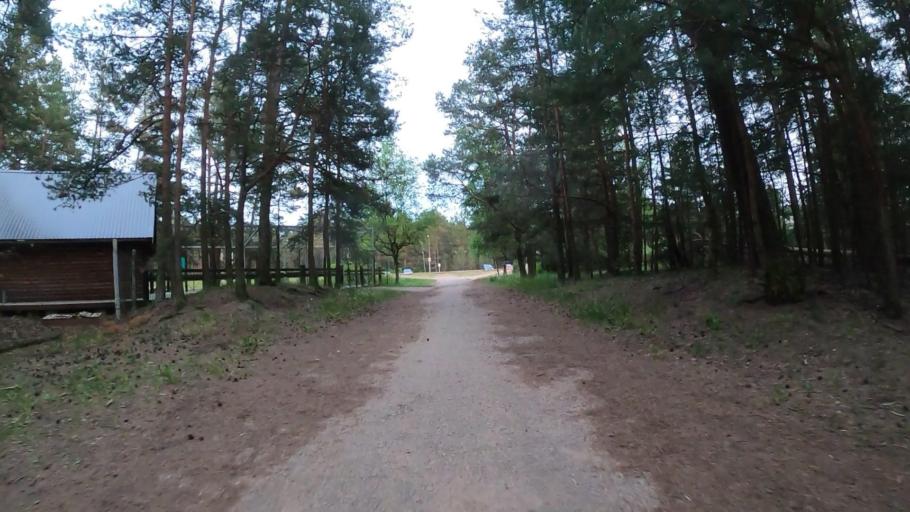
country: LV
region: Riga
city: Jaunciems
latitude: 57.0869
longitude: 24.1527
